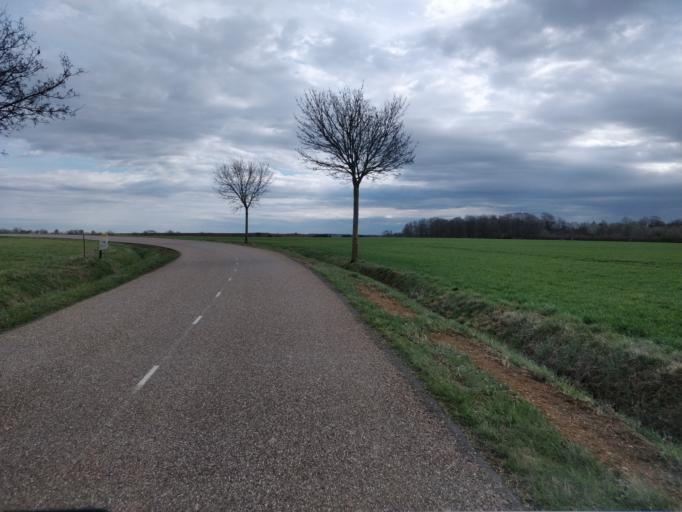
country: FR
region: Lorraine
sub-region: Departement de Meurthe-et-Moselle
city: Doncourt-les-Conflans
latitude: 49.1051
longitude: 5.8953
